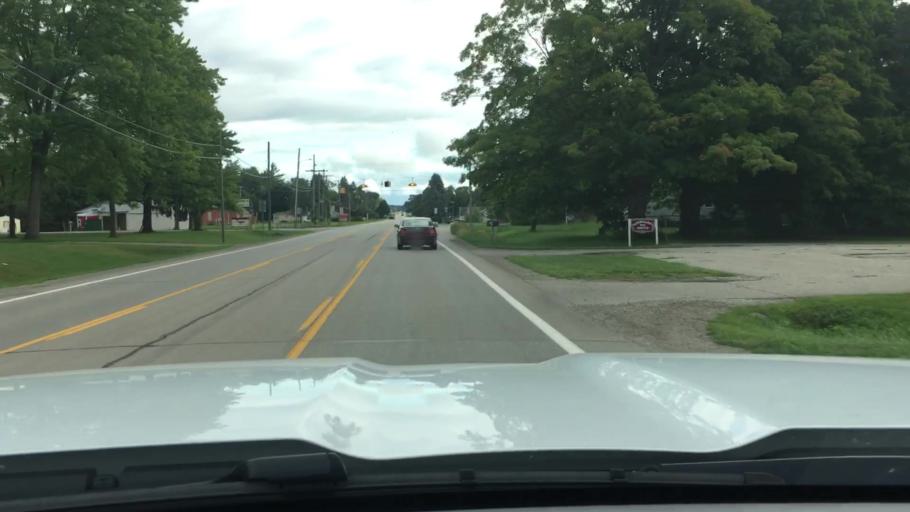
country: US
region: Michigan
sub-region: Tuscola County
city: Caro
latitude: 43.5095
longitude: -83.3694
